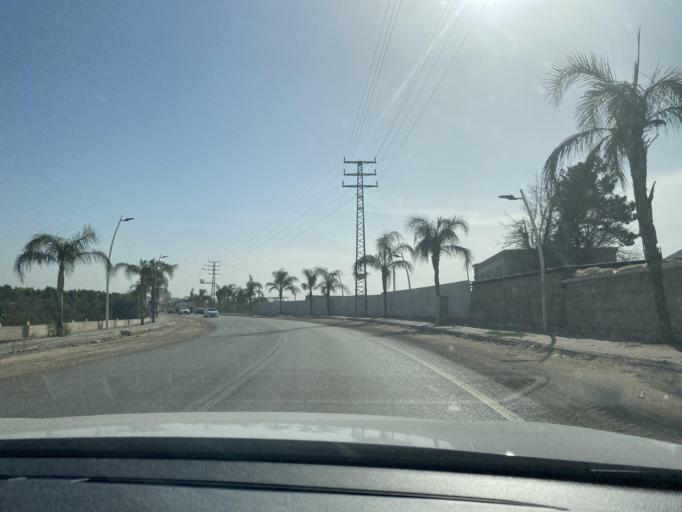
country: IL
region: Central District
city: Jaljulya
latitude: 32.1381
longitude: 34.9618
